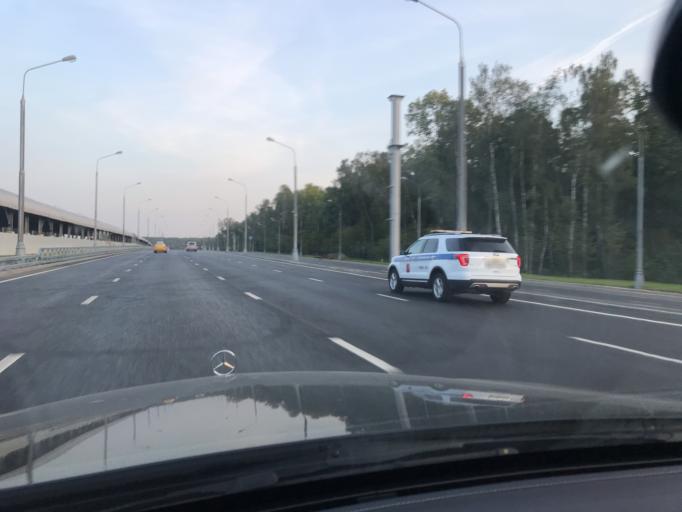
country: RU
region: Moskovskaya
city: Mosrentgen
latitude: 55.5954
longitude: 37.4169
